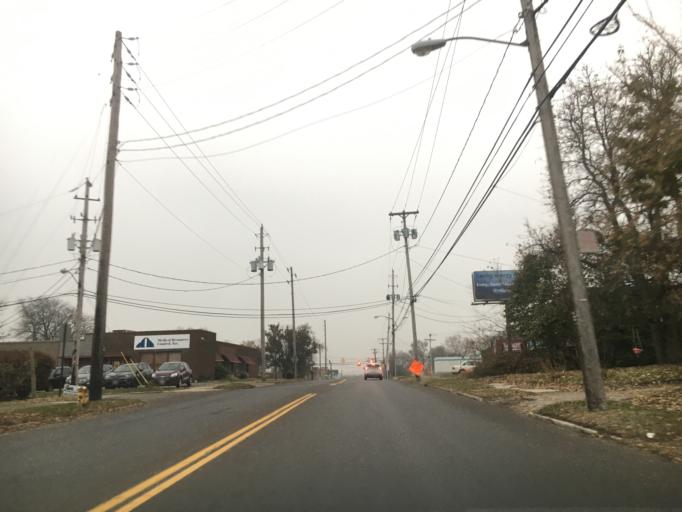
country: US
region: Ohio
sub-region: Summit County
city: Akron
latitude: 41.0958
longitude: -81.4881
